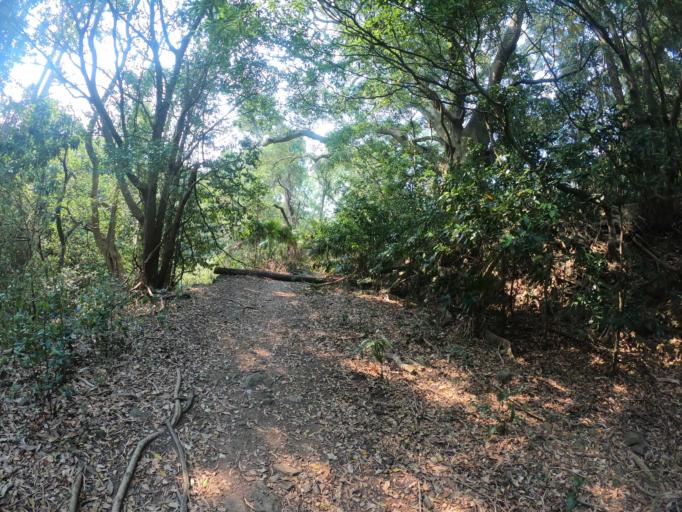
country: AU
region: New South Wales
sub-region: Wollongong
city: Bulli
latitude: -34.2886
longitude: 150.9043
